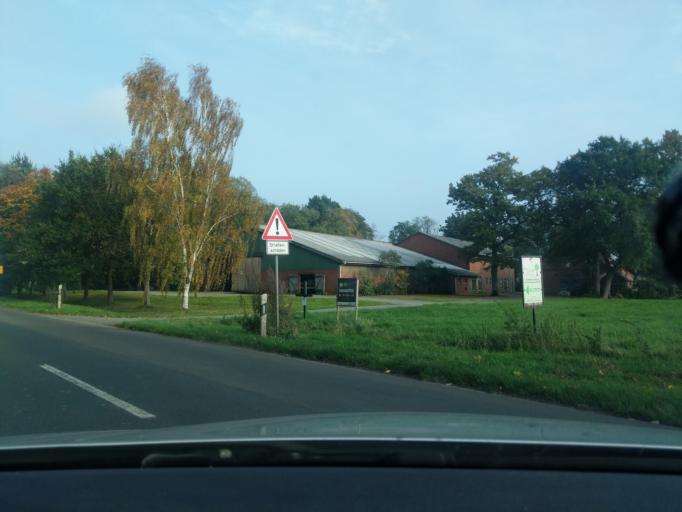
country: DE
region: Lower Saxony
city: Mittelstenahe
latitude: 53.6485
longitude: 9.0309
